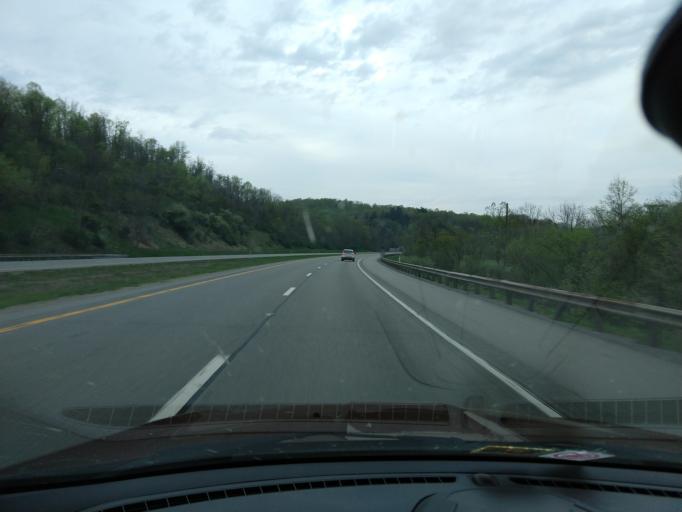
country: US
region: West Virginia
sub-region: Lewis County
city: Weston
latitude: 39.0680
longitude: -80.4041
